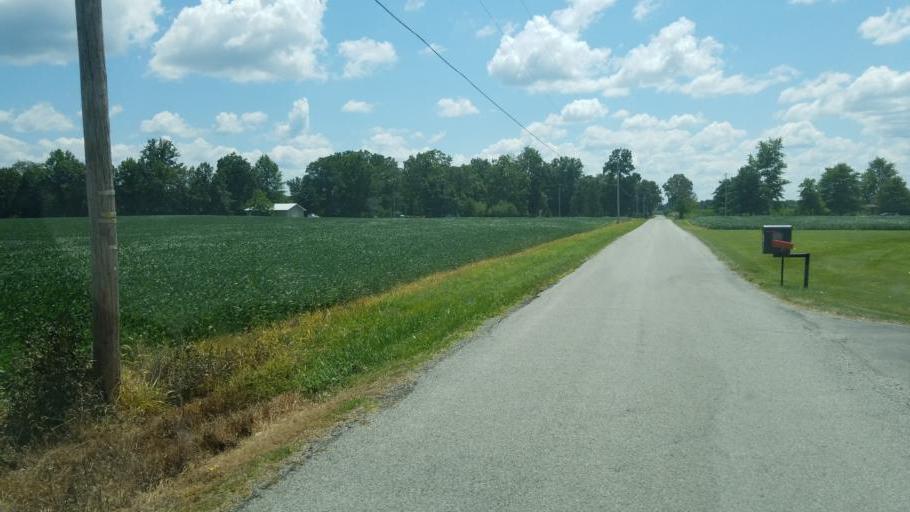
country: US
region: Ohio
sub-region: Marion County
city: Marion
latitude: 40.6800
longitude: -83.1102
